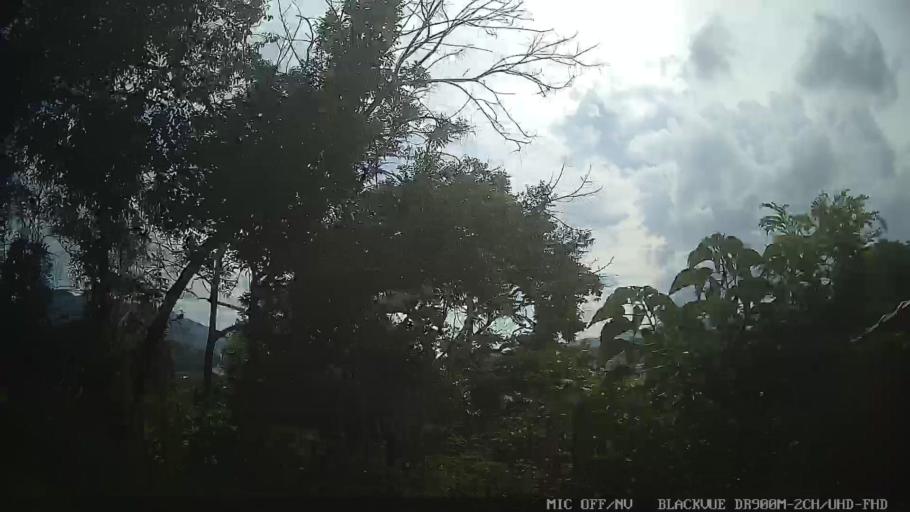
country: BR
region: Minas Gerais
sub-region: Extrema
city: Extrema
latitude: -22.8270
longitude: -46.2830
